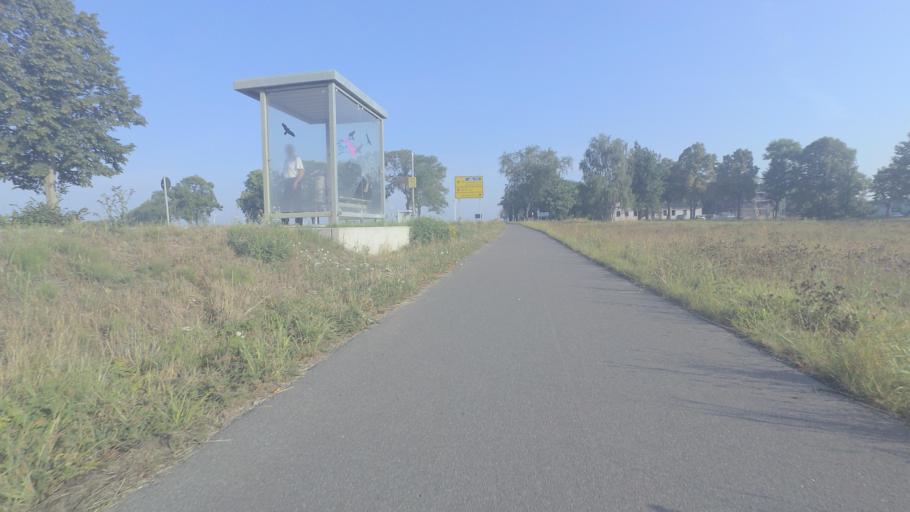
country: DE
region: Mecklenburg-Vorpommern
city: Gormin
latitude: 53.9963
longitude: 13.1474
